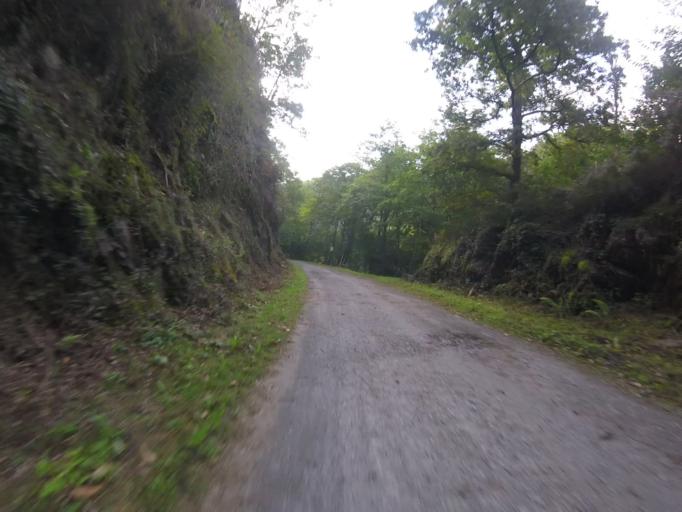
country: ES
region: Basque Country
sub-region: Provincia de Guipuzcoa
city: Berastegui
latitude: 43.1497
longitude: -1.9643
